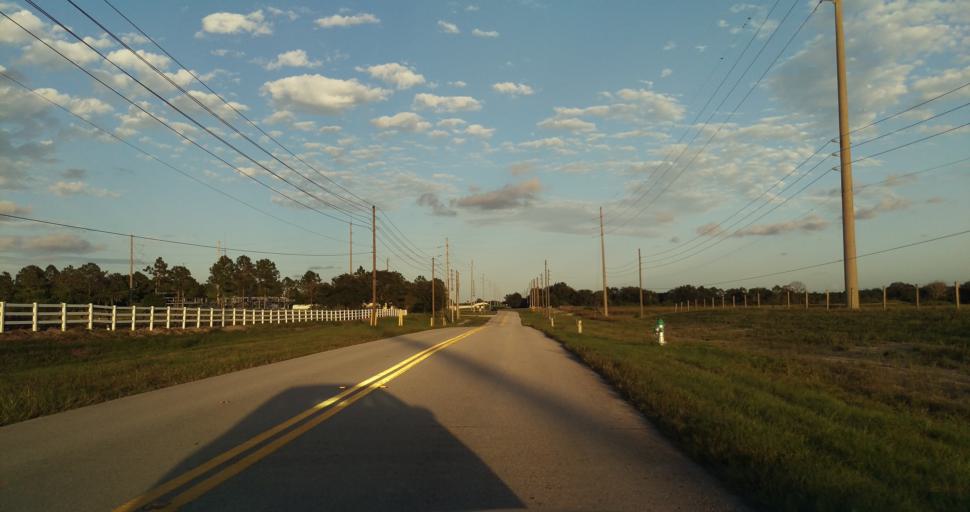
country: US
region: Florida
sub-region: Polk County
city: Citrus Ridge
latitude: 28.4416
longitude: -81.6339
